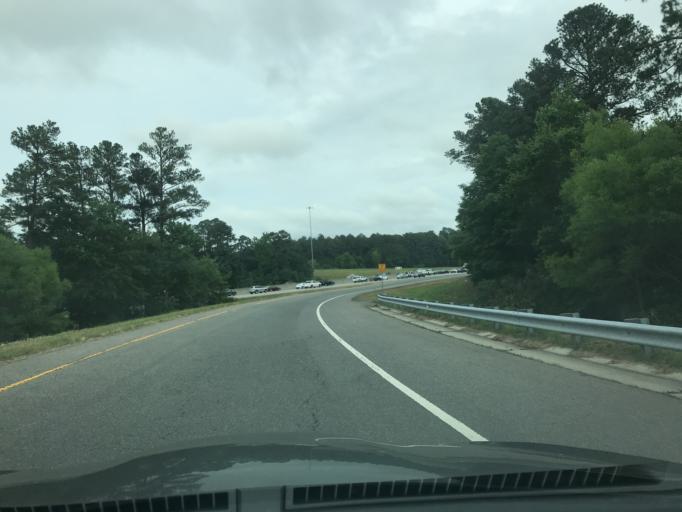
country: US
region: North Carolina
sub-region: Wake County
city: Morrisville
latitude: 35.8711
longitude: -78.8310
